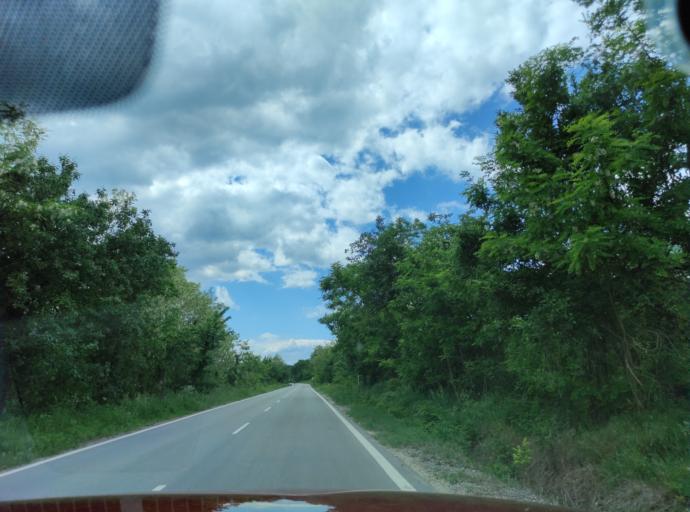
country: BG
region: Montana
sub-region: Obshtina Chiprovtsi
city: Chiprovtsi
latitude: 43.4453
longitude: 22.9240
